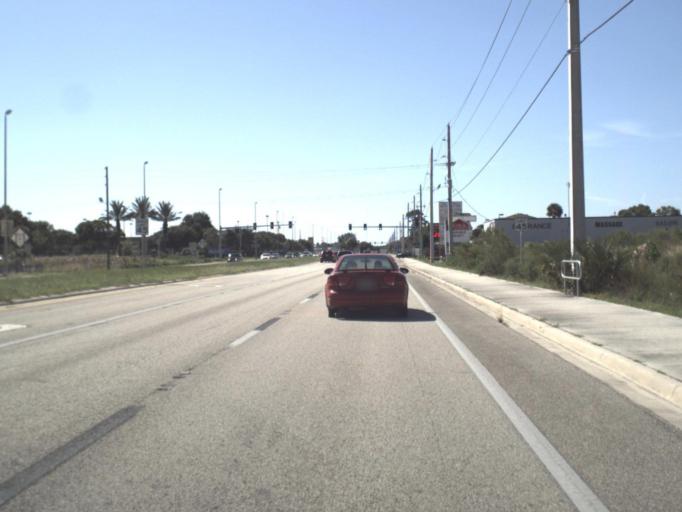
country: US
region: Florida
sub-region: Charlotte County
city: Grove City
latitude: 26.9346
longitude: -82.3078
